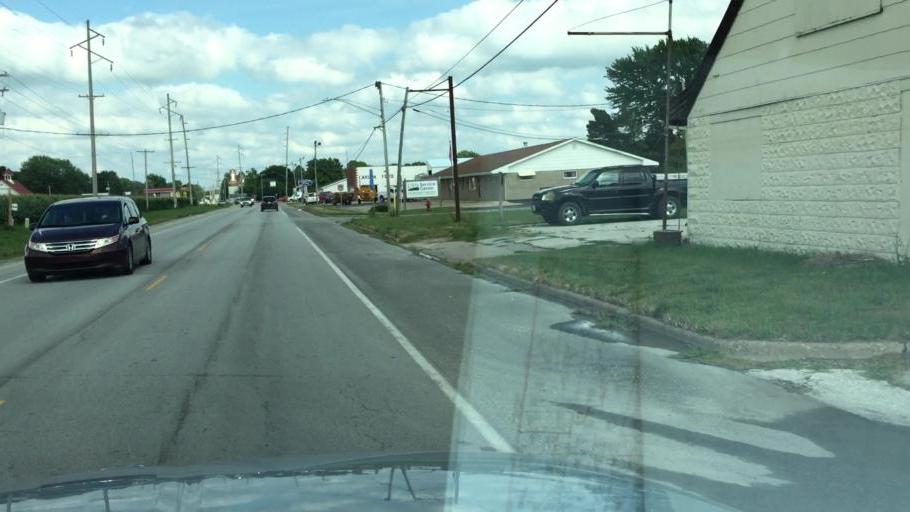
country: US
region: Illinois
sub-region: Hancock County
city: Carthage
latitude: 40.4161
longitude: -91.1459
